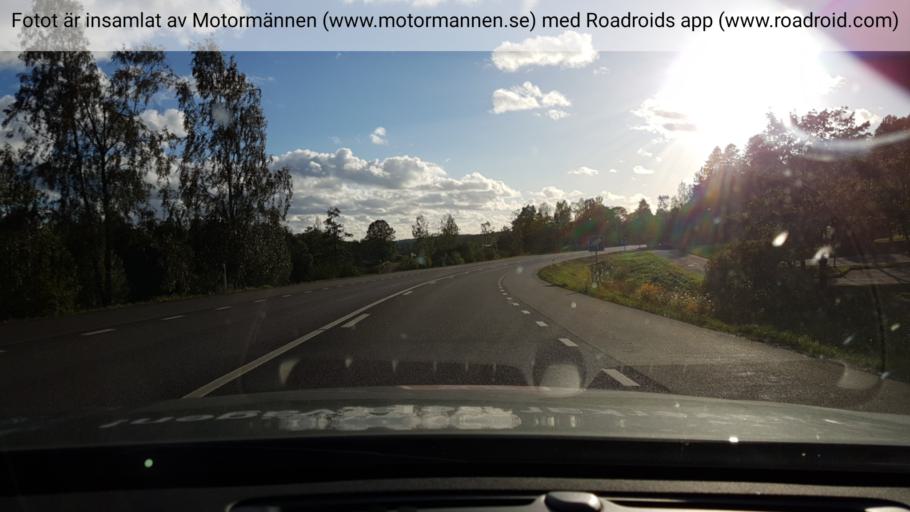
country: SE
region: Vaermland
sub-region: Karlstads Kommun
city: Molkom
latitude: 59.5985
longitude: 13.7354
